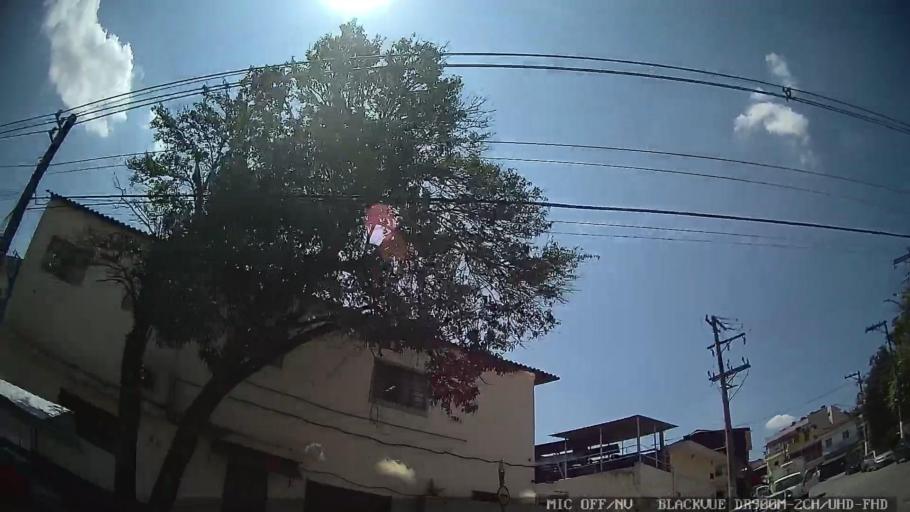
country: BR
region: Sao Paulo
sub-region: Guarulhos
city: Guarulhos
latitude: -23.5232
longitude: -46.4927
